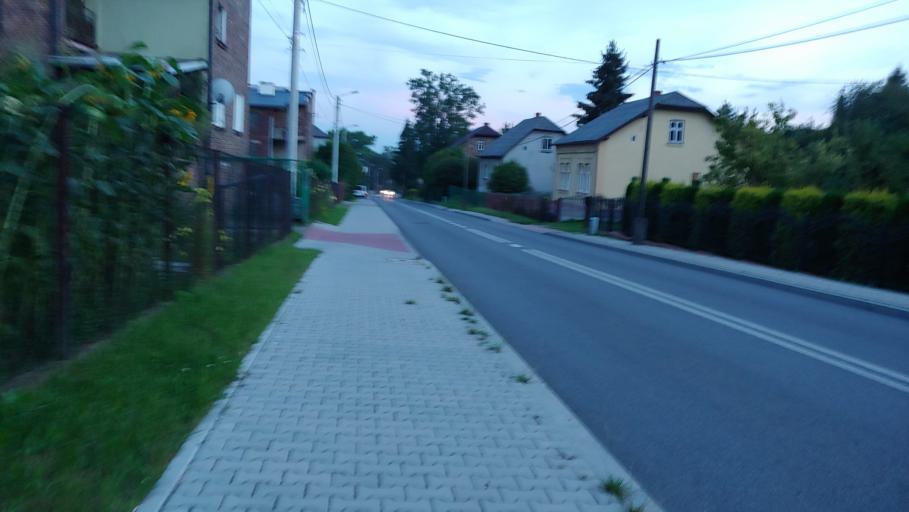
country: PL
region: Lesser Poland Voivodeship
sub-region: Powiat chrzanowski
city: Trzebinia
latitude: 50.1672
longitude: 19.4585
